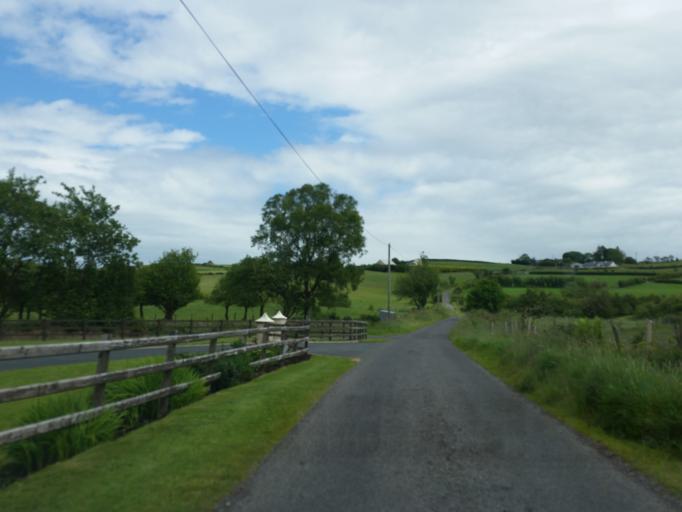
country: GB
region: Northern Ireland
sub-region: Omagh District
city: Omagh
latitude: 54.5584
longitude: -7.0669
